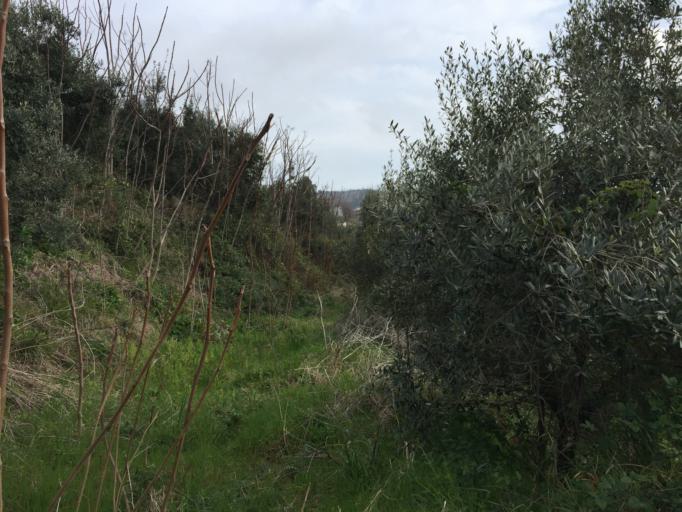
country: IT
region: Campania
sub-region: Provincia di Napoli
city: Pozzuoli
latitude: 40.8330
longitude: 14.1289
